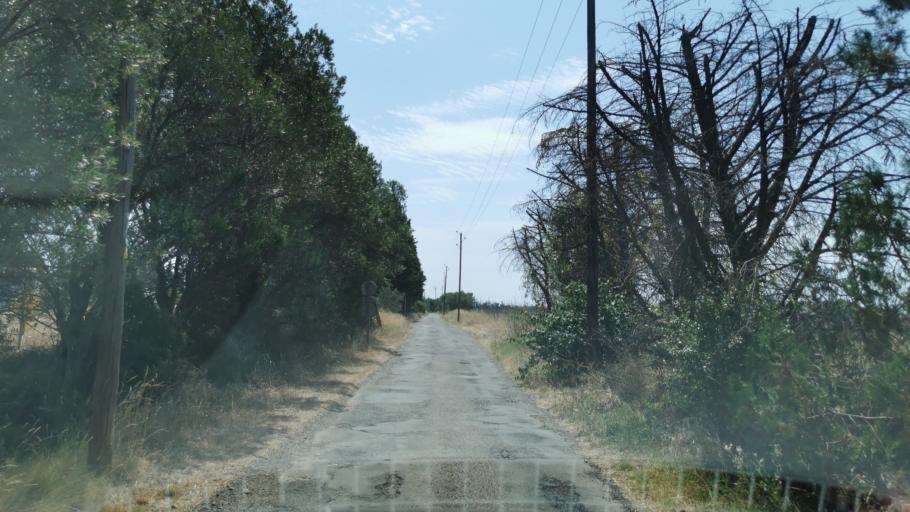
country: FR
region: Languedoc-Roussillon
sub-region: Departement de l'Aude
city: Bize-Minervois
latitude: 43.2941
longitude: 2.8832
